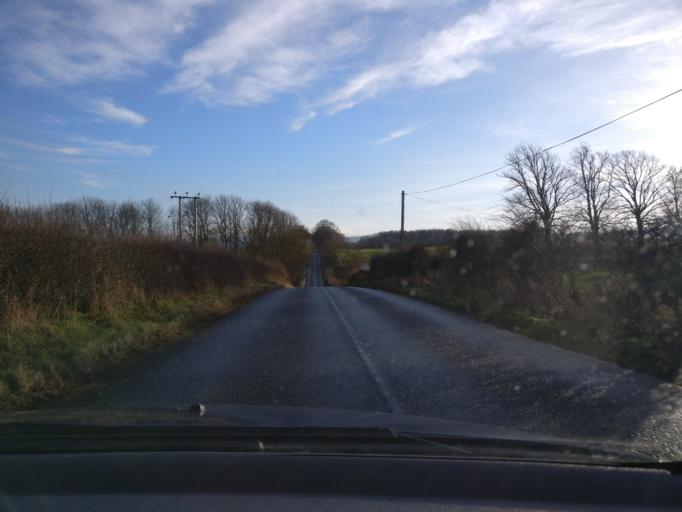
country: GB
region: Scotland
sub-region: The Scottish Borders
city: Kelso
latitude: 55.5294
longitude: -2.4319
